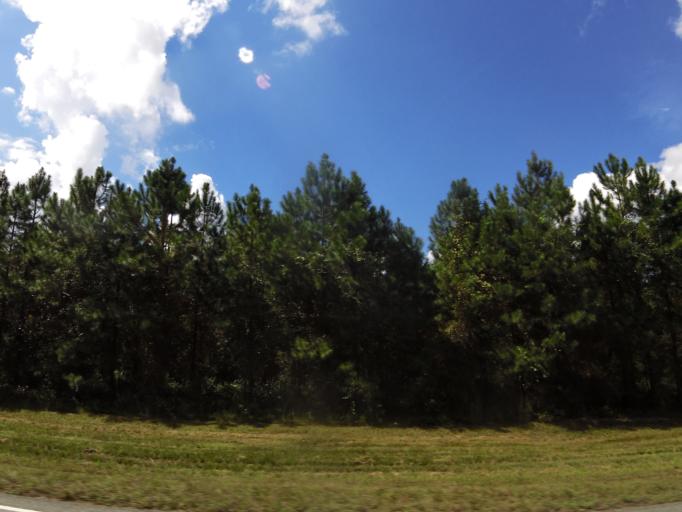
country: US
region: Georgia
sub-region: Charlton County
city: Folkston
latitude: 30.9893
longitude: -82.0259
